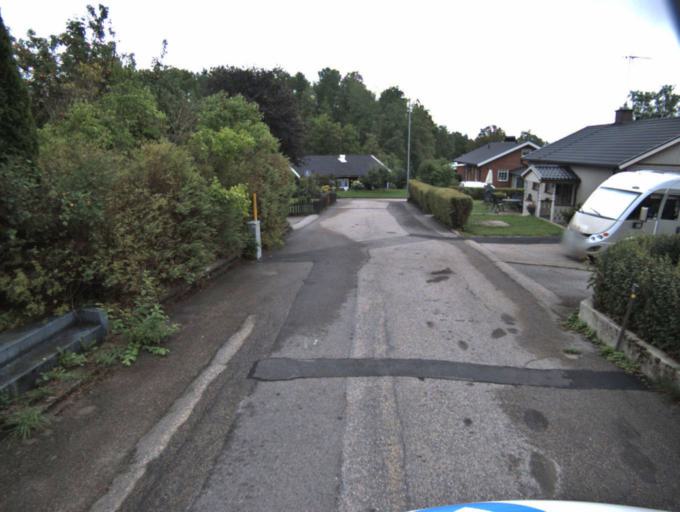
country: SE
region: Vaestra Goetaland
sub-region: Tranemo Kommun
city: Langhem
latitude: 57.7007
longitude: 13.2968
